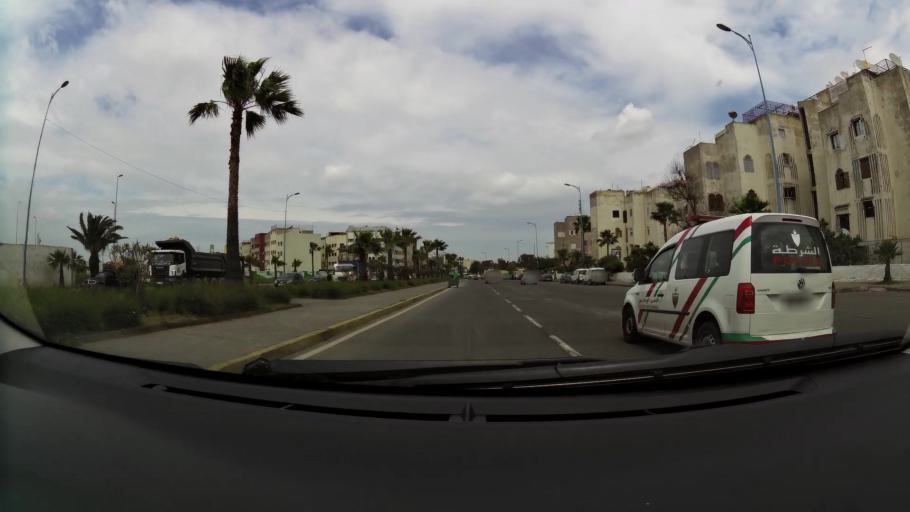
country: MA
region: Grand Casablanca
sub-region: Casablanca
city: Casablanca
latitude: 33.5814
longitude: -7.5702
